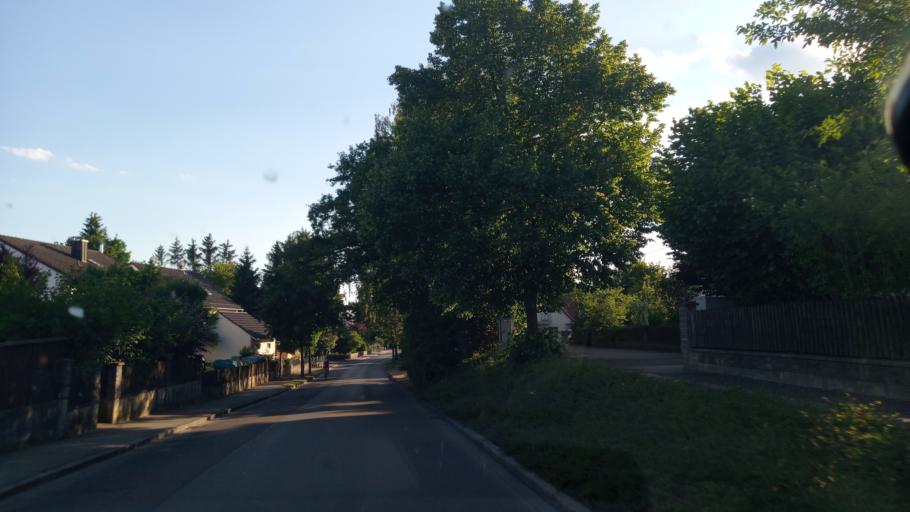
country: DE
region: Bavaria
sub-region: Upper Bavaria
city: Weichs
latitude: 48.3784
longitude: 11.4100
